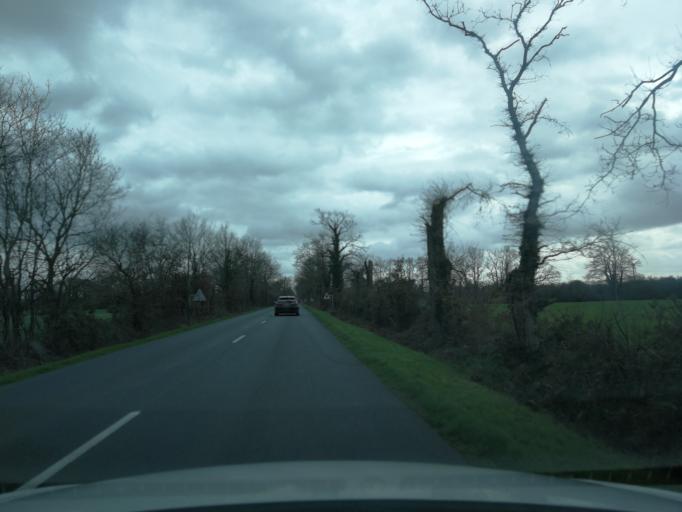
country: FR
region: Pays de la Loire
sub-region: Departement de la Loire-Atlantique
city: Montbert
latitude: 47.0201
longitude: -1.4885
